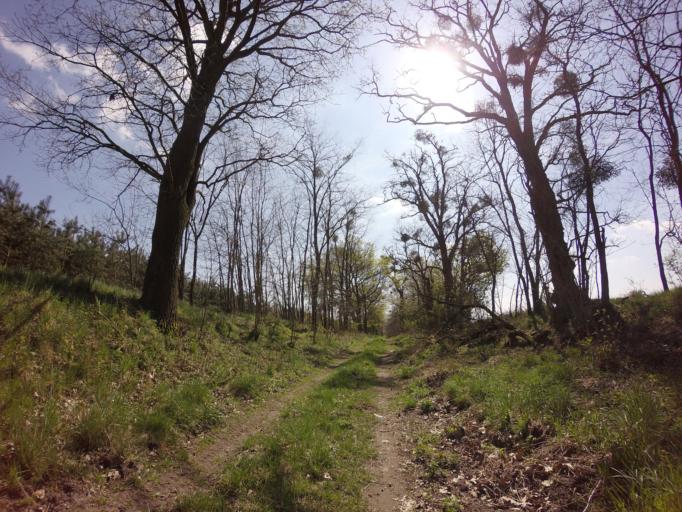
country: PL
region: West Pomeranian Voivodeship
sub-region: Powiat stargardzki
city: Suchan
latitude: 53.2124
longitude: 15.3032
